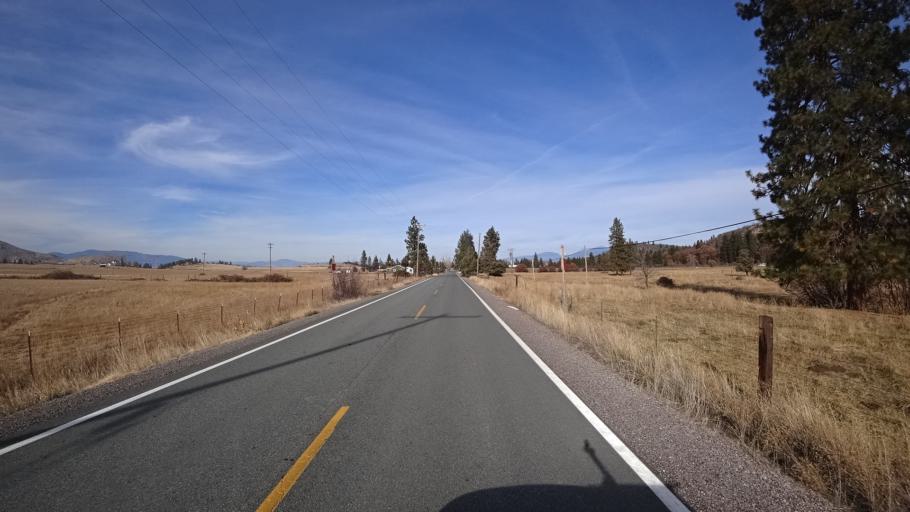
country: US
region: California
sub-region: Siskiyou County
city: Weed
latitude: 41.4364
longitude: -122.4359
